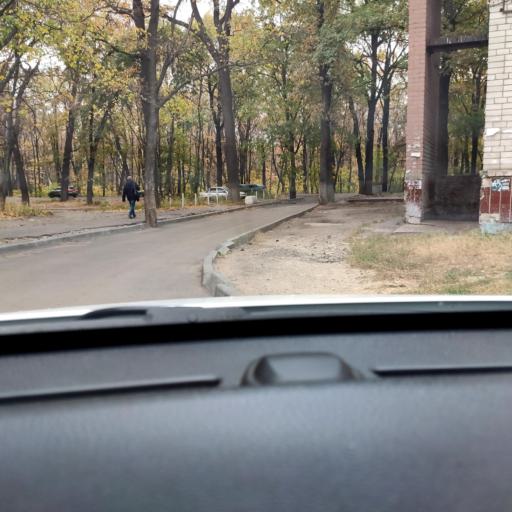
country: RU
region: Voronezj
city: Voronezh
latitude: 51.7210
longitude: 39.2222
